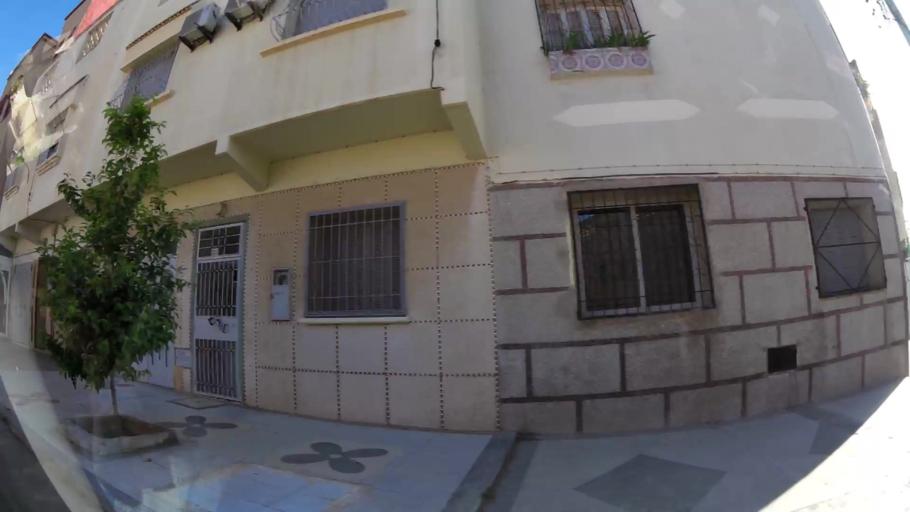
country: MA
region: Oriental
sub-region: Oujda-Angad
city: Oujda
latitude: 34.6943
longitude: -1.9155
